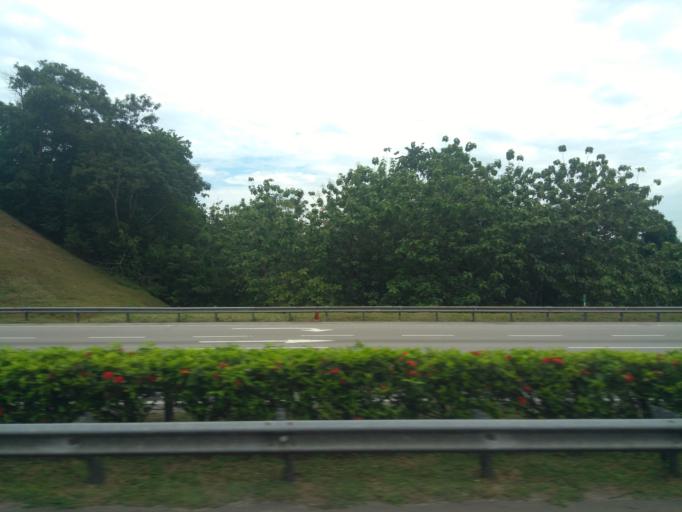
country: MY
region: Melaka
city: Pulau Sebang
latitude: 2.4446
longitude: 102.1866
